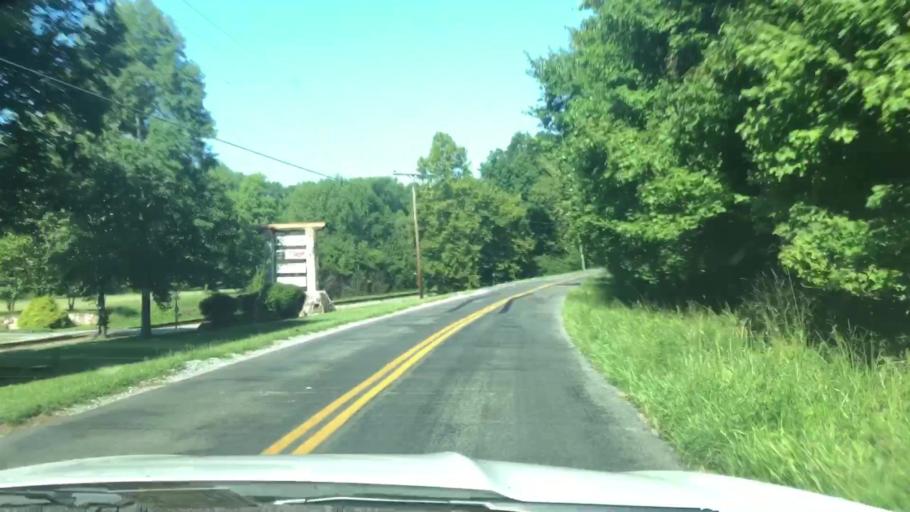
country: US
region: Virginia
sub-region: New Kent County
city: New Kent
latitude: 37.4144
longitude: -76.9365
